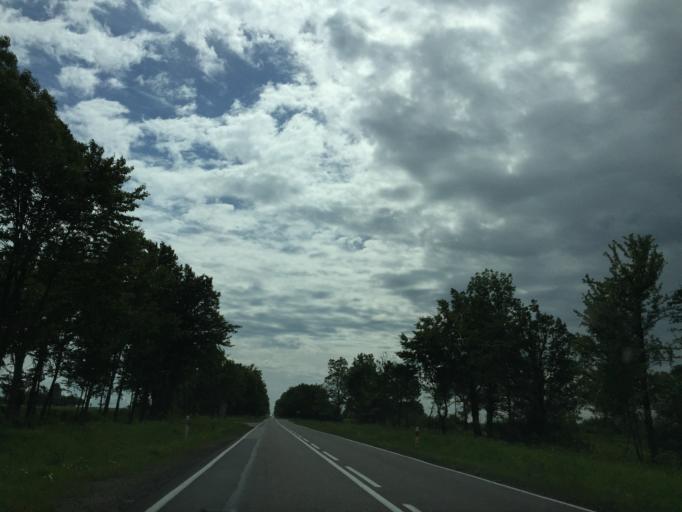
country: PL
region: Podlasie
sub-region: Powiat bielski
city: Bocki
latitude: 52.6230
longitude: 23.0037
